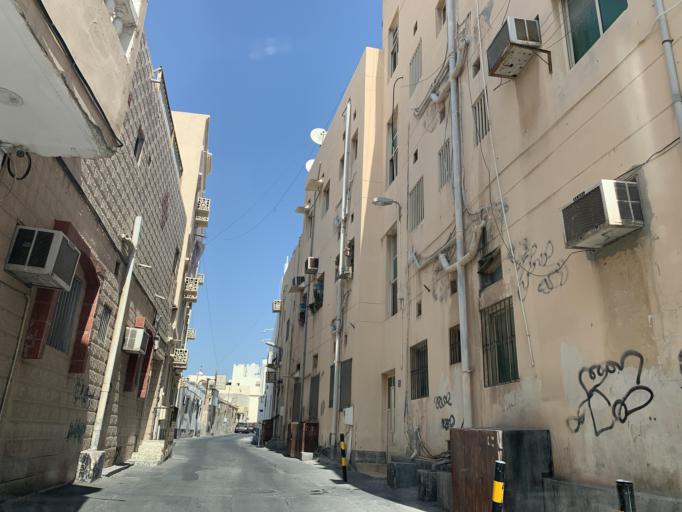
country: BH
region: Muharraq
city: Al Muharraq
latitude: 26.2530
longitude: 50.6154
